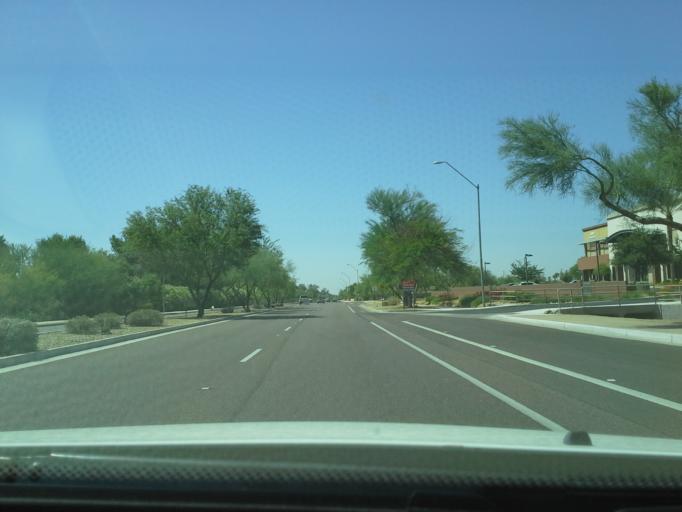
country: US
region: Arizona
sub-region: Maricopa County
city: Paradise Valley
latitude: 33.6130
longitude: -111.9086
